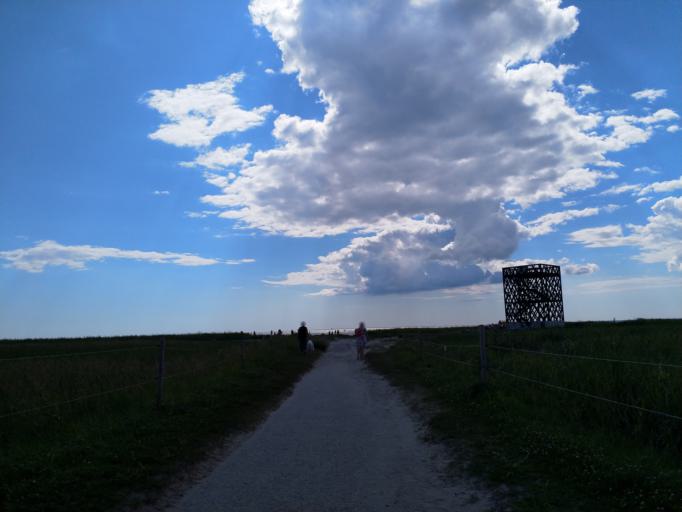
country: EE
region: Paernumaa
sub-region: Paernu linn
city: Parnu
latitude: 58.3664
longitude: 24.5277
